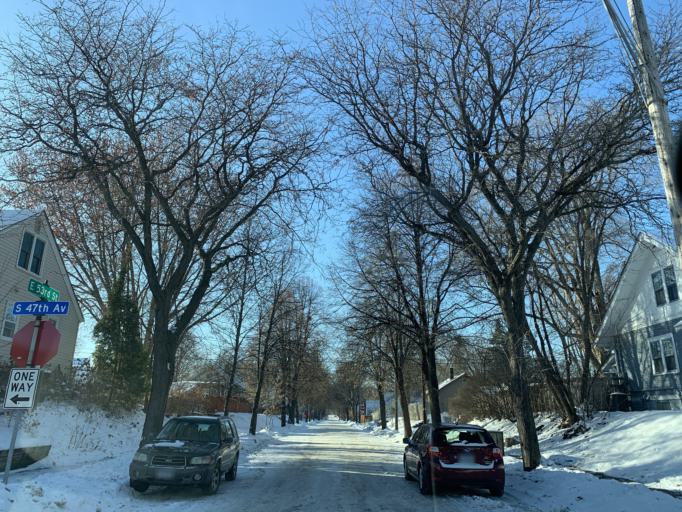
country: US
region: Minnesota
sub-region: Dakota County
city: Mendota Heights
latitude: 44.9073
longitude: -93.2063
